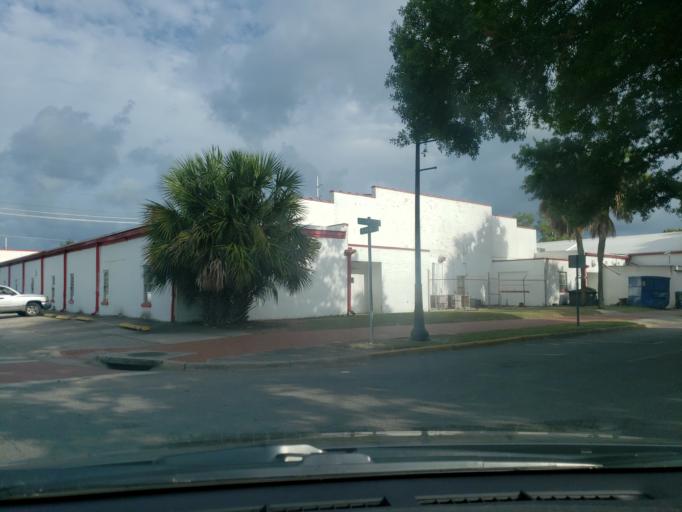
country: US
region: Georgia
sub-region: Chatham County
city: Savannah
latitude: 32.0517
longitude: -81.1079
